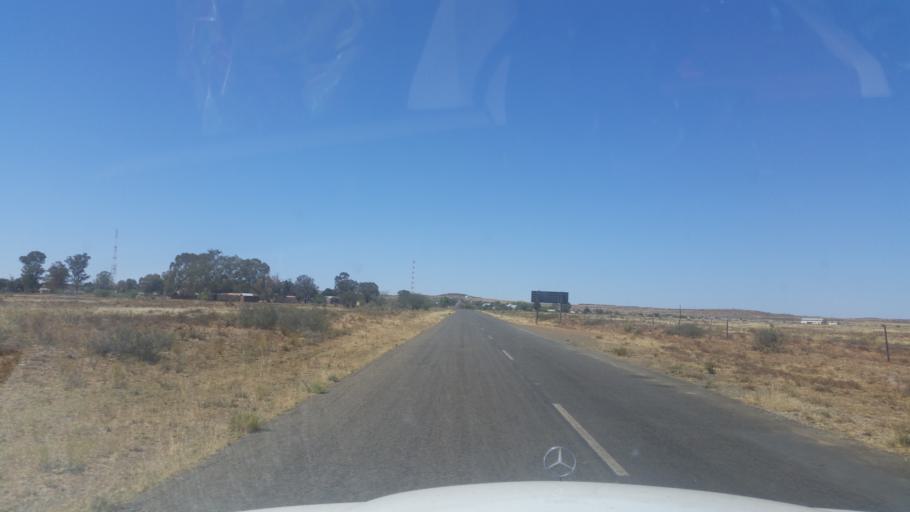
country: ZA
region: Eastern Cape
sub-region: Joe Gqabi District Municipality
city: Burgersdorp
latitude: -30.7709
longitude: 25.7918
